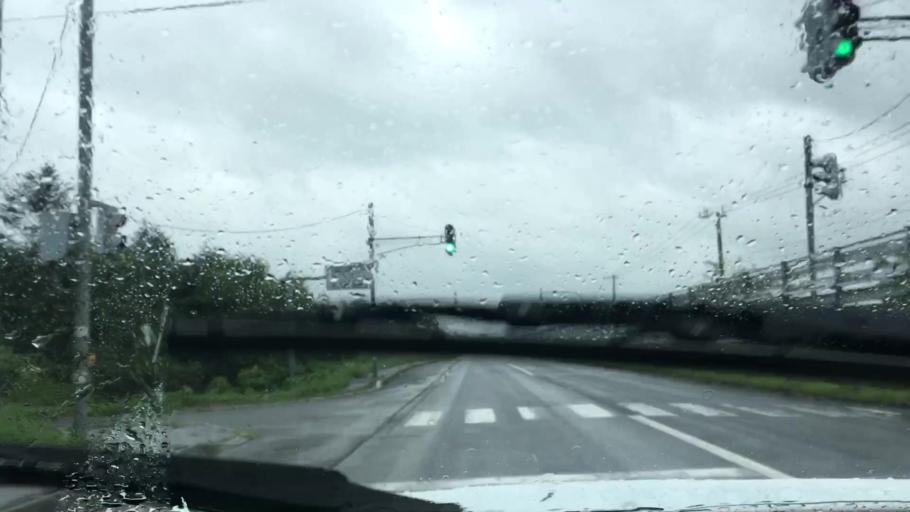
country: JP
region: Hokkaido
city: Nanae
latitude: 42.3082
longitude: 140.2727
